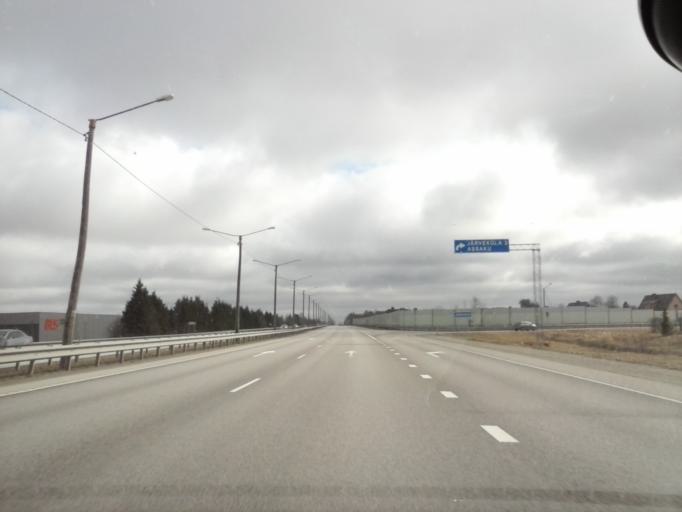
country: EE
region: Harju
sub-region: Rae vald
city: Jueri
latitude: 59.3815
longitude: 24.8387
